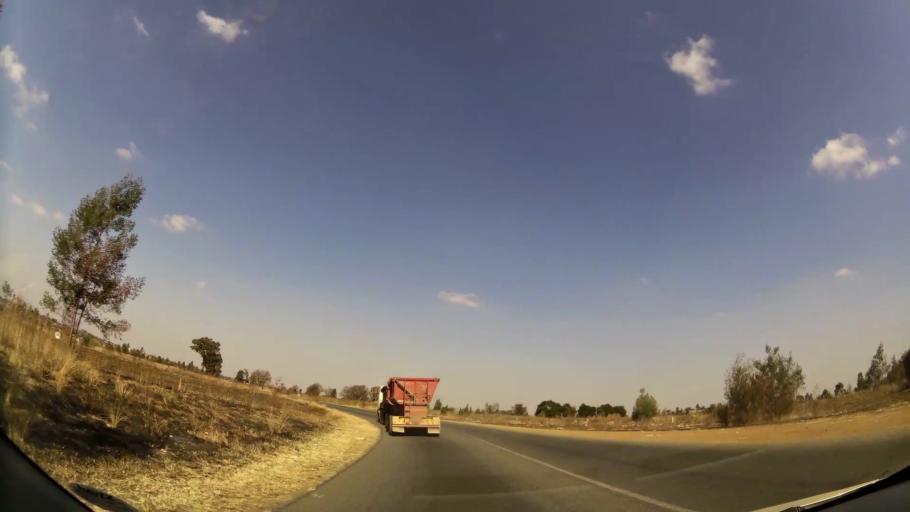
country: ZA
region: Gauteng
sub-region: West Rand District Municipality
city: Krugersdorp
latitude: -26.1297
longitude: 27.8140
